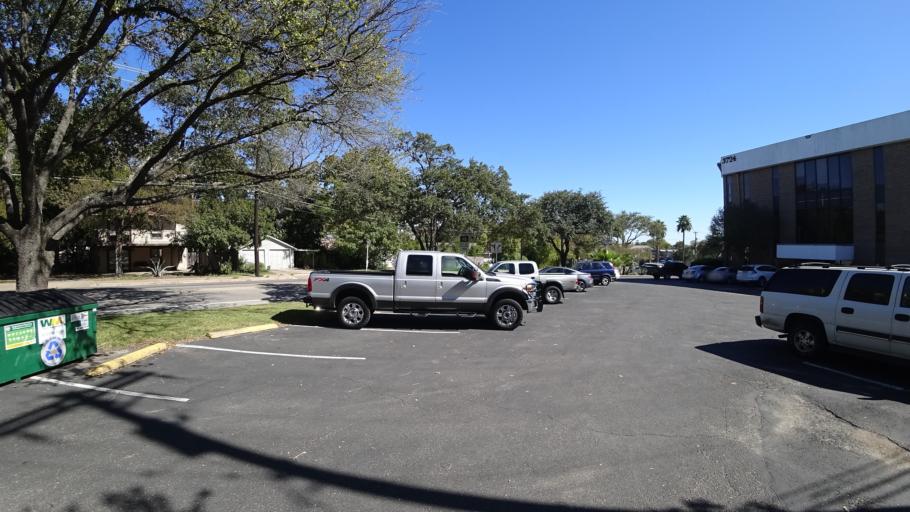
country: US
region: Texas
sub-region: Travis County
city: Austin
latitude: 30.3099
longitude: -97.7514
